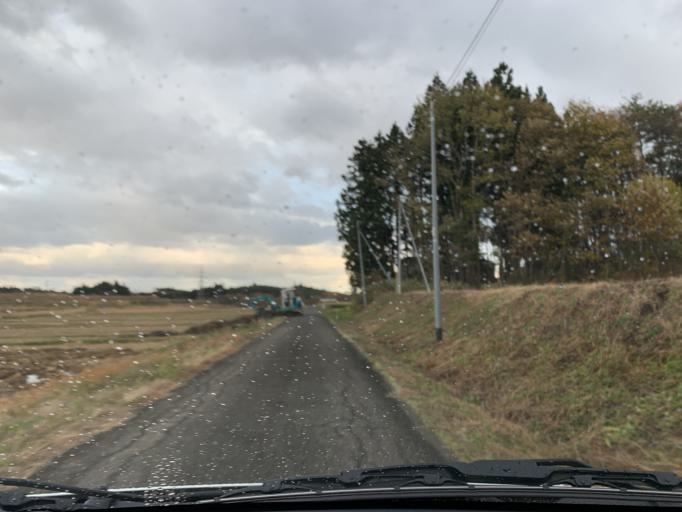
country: JP
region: Iwate
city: Mizusawa
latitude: 39.0868
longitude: 141.0014
